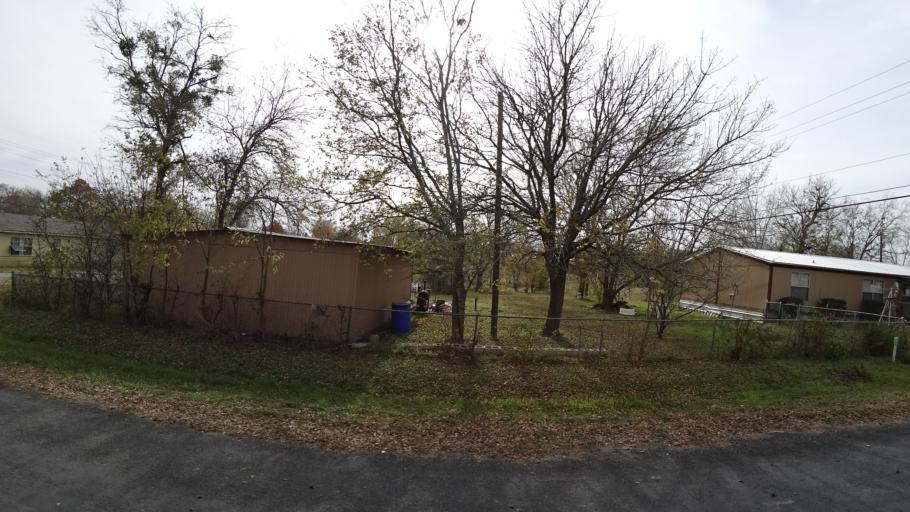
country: US
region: Texas
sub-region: Travis County
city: Garfield
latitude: 30.1314
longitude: -97.6148
